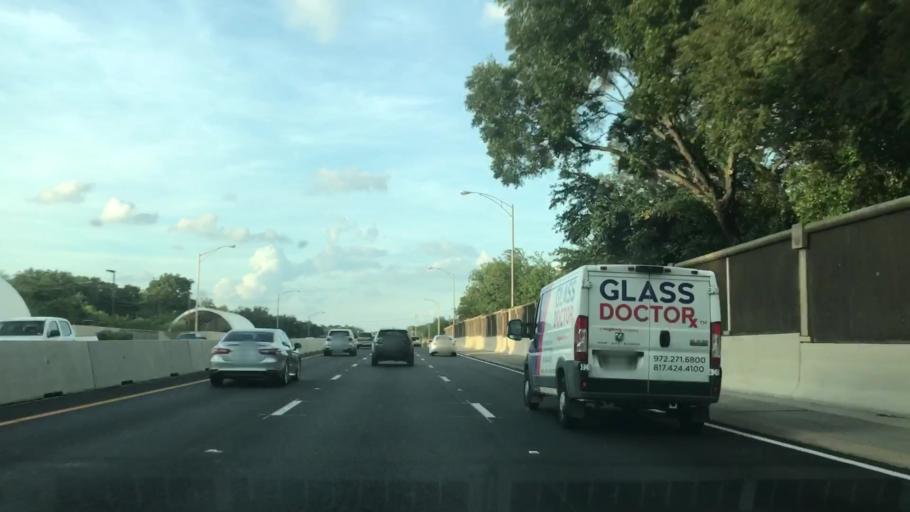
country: US
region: Texas
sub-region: Dallas County
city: University Park
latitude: 32.8837
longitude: -96.8091
